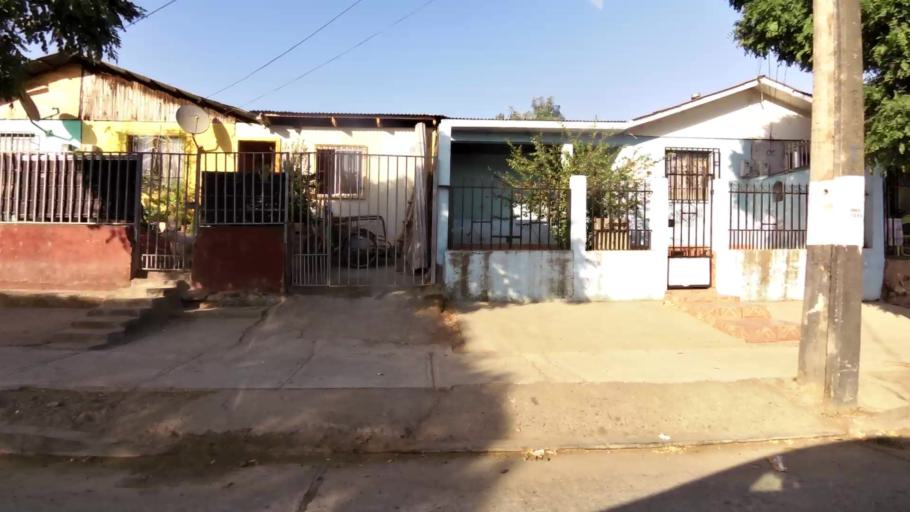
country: CL
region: Maule
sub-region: Provincia de Talca
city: Talca
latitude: -35.4085
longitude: -71.6500
